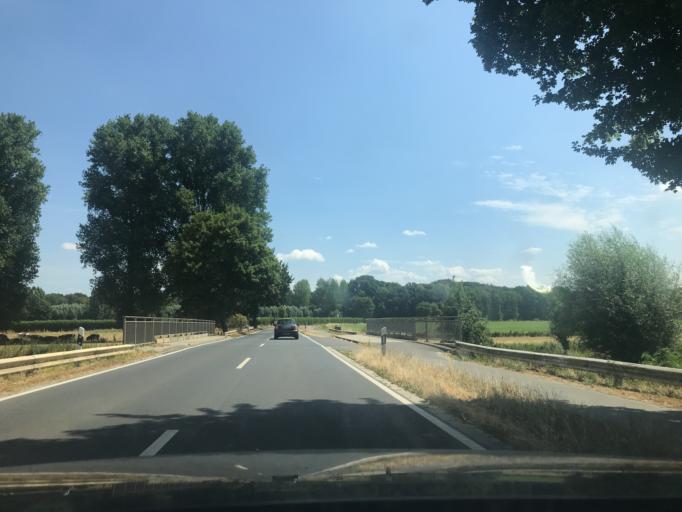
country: DE
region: North Rhine-Westphalia
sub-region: Regierungsbezirk Dusseldorf
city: Wachtendonk
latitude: 51.3757
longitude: 6.3567
